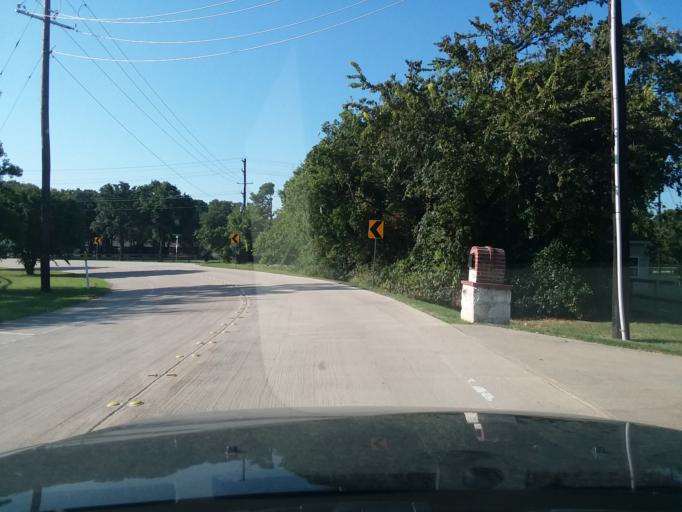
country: US
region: Texas
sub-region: Denton County
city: Copper Canyon
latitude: 33.1110
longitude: -97.0963
